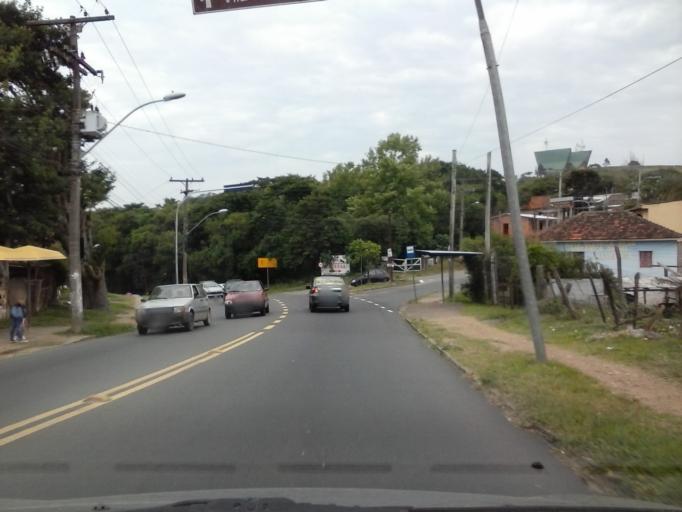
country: BR
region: Rio Grande do Sul
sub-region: Porto Alegre
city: Porto Alegre
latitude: -30.0963
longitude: -51.1778
